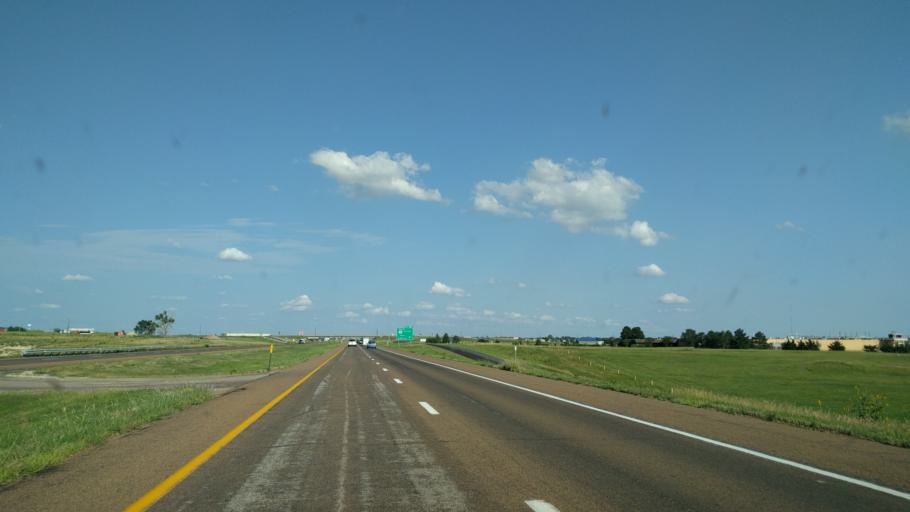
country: US
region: Kansas
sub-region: Ellis County
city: Hays
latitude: 38.9150
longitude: -99.3621
